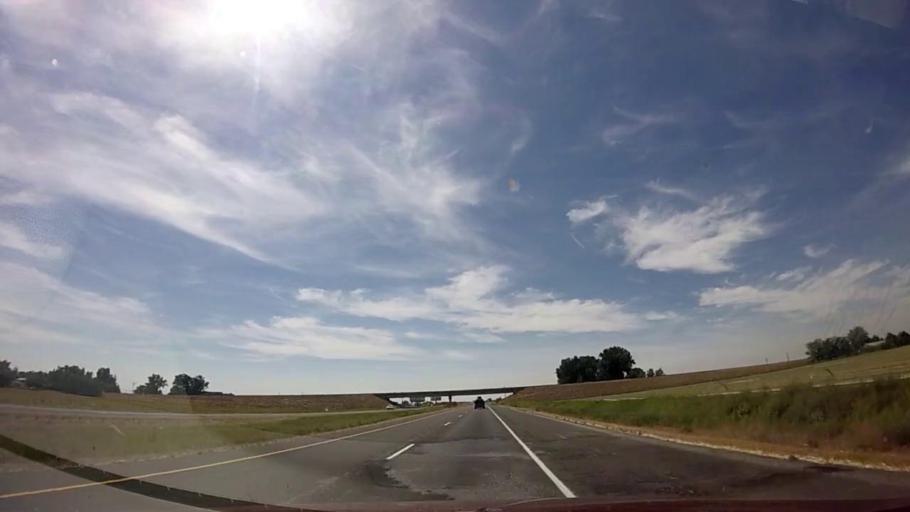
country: US
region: Idaho
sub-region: Minidoka County
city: Rupert
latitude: 42.5690
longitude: -113.7031
